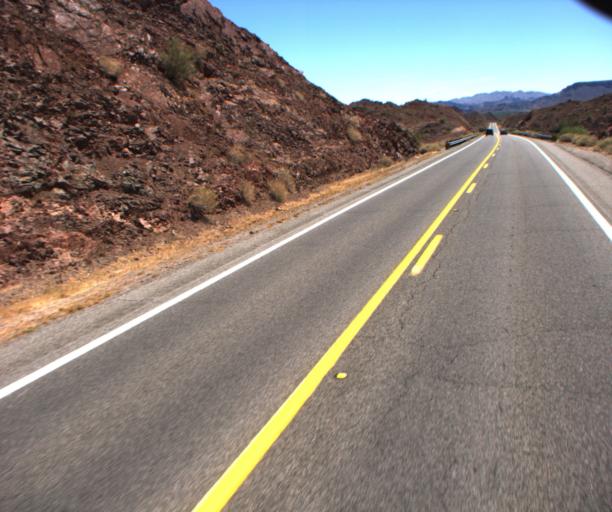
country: US
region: Arizona
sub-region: La Paz County
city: Cienega Springs
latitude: 34.3168
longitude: -114.1133
